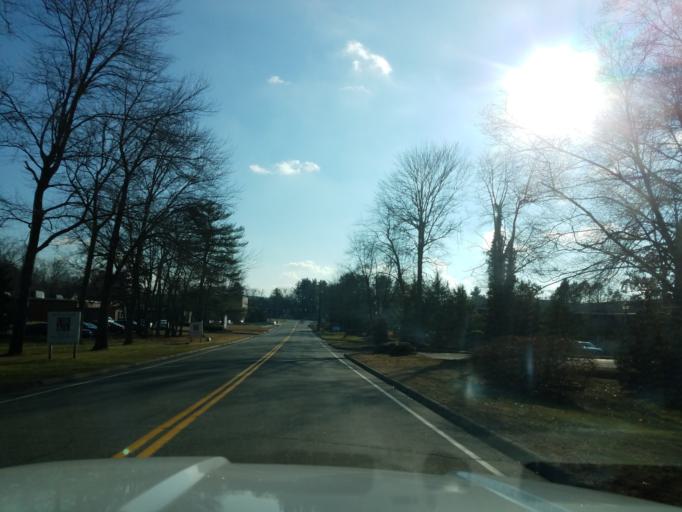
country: US
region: Connecticut
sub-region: Hartford County
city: Glastonbury Center
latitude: 41.7181
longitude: -72.5855
